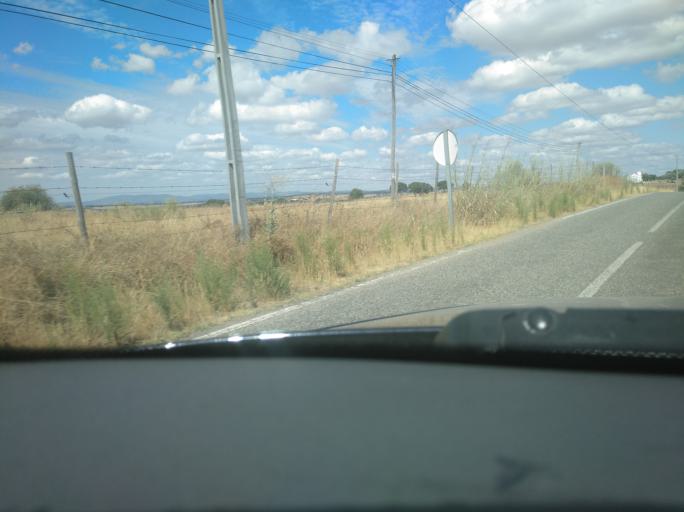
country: PT
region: Portalegre
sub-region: Arronches
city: Arronches
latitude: 39.0623
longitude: -7.4101
